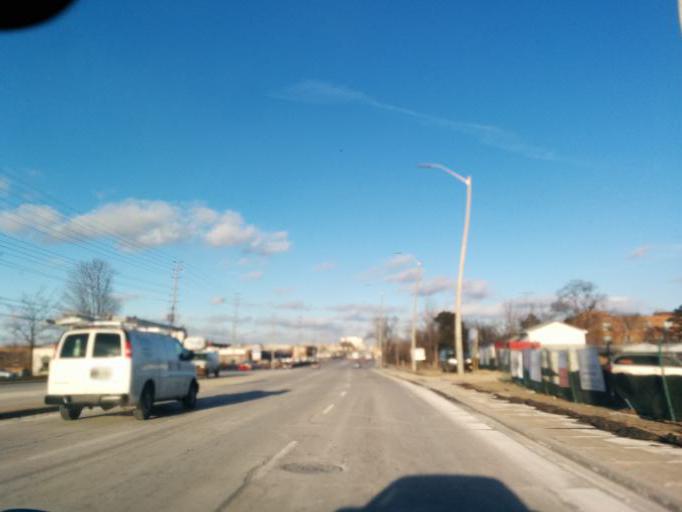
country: CA
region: Ontario
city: Mississauga
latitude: 43.6276
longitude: -79.6295
